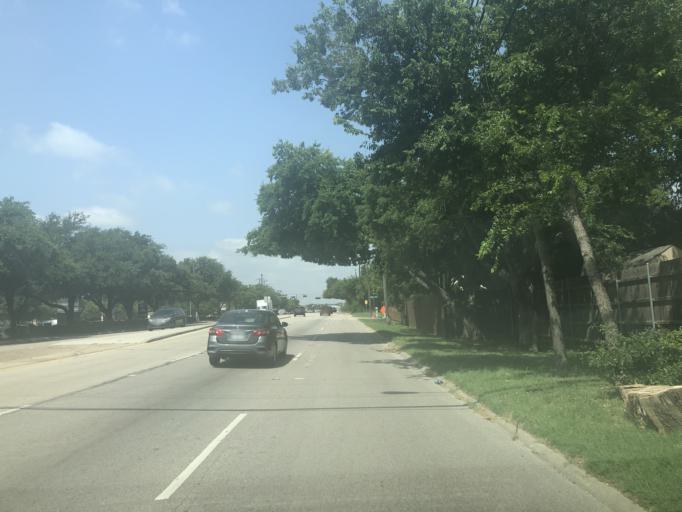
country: US
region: Texas
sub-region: Dallas County
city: University Park
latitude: 32.8627
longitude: -96.8493
